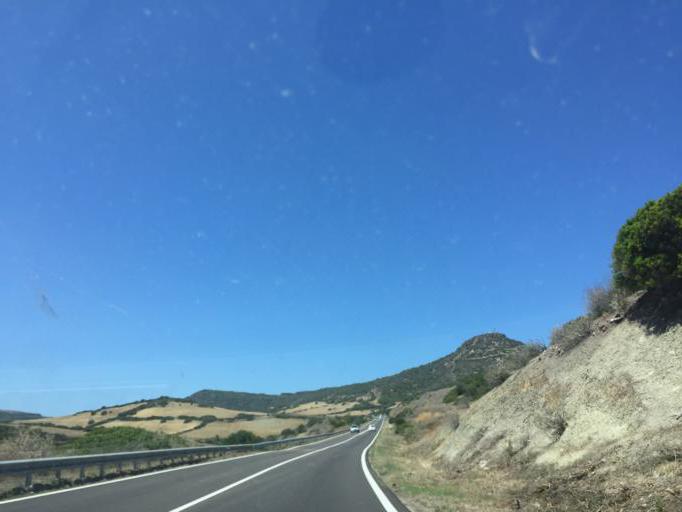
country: IT
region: Sardinia
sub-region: Provincia di Sassari
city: Valledoria
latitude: 40.9021
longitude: 8.7881
